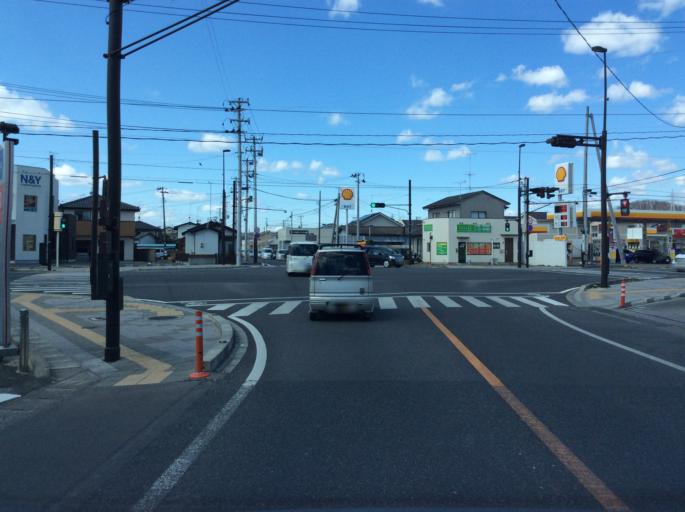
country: JP
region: Fukushima
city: Iwaki
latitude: 36.9578
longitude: 140.9041
